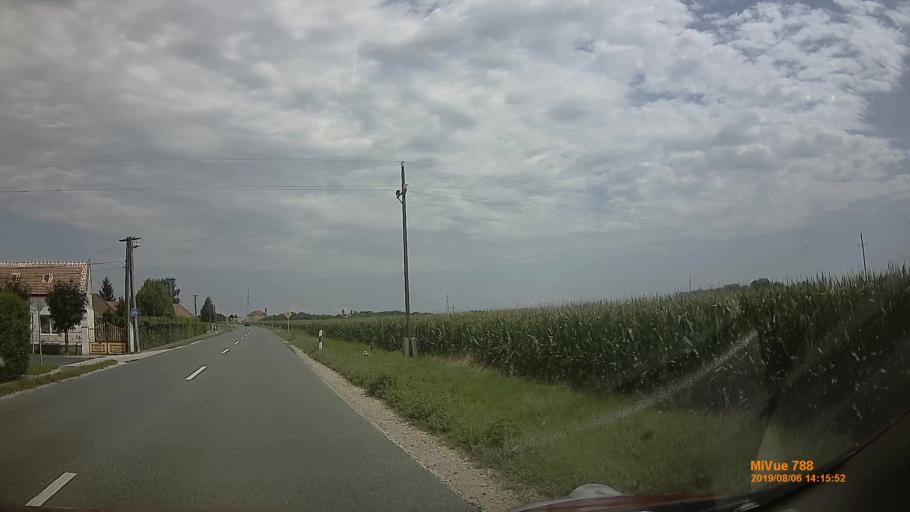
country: HU
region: Vas
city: Taplanszentkereszt
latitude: 47.1909
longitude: 16.7068
